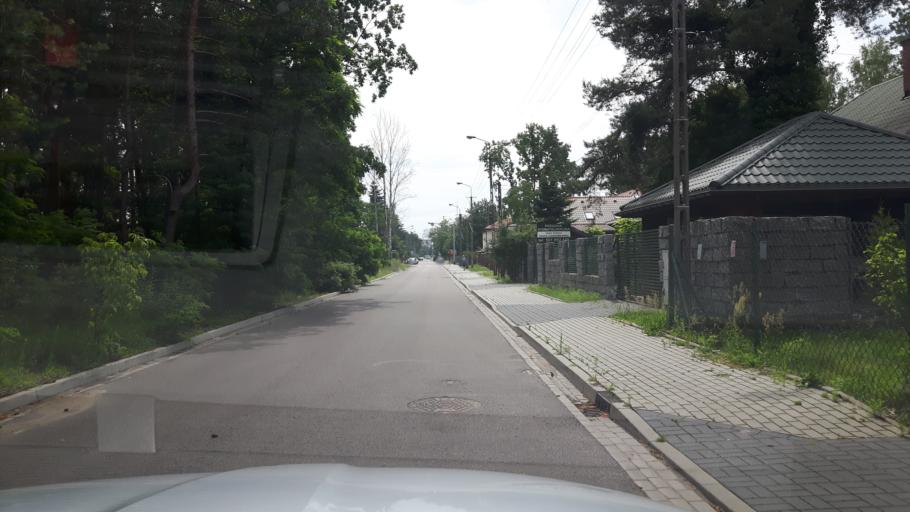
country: PL
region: Masovian Voivodeship
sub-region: Powiat wolominski
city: Wolomin
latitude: 52.3509
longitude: 21.2230
